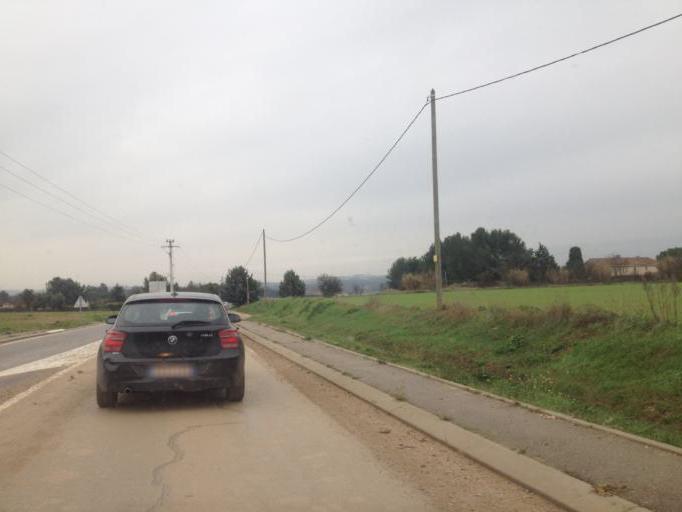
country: FR
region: Provence-Alpes-Cote d'Azur
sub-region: Departement des Bouches-du-Rhone
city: Eguilles
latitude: 43.5202
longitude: 5.3517
